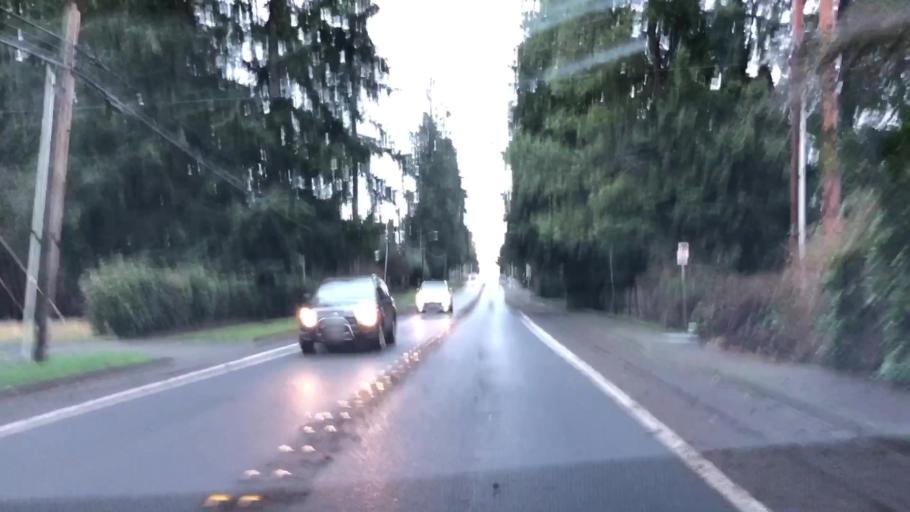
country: US
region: Washington
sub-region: King County
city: Redmond
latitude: 47.6754
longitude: -122.1582
